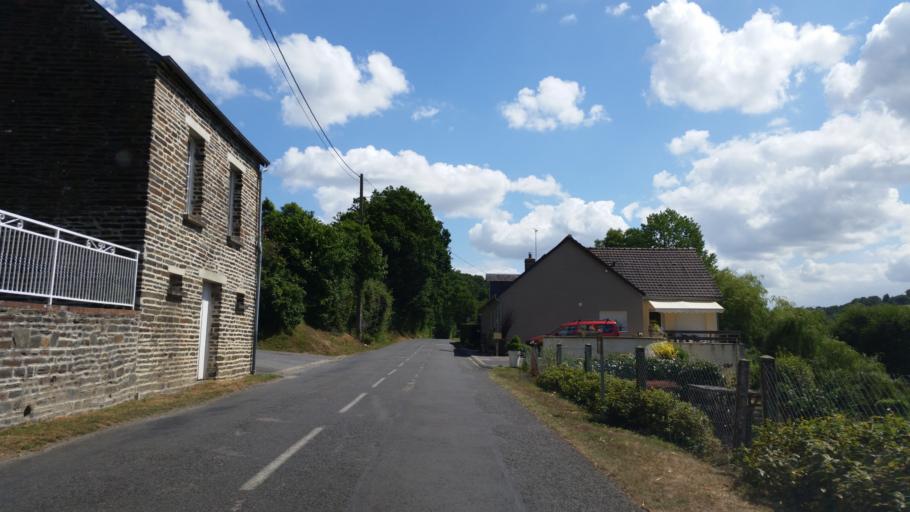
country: FR
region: Lower Normandy
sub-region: Departement du Calvados
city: Clecy
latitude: 48.8564
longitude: -0.3957
